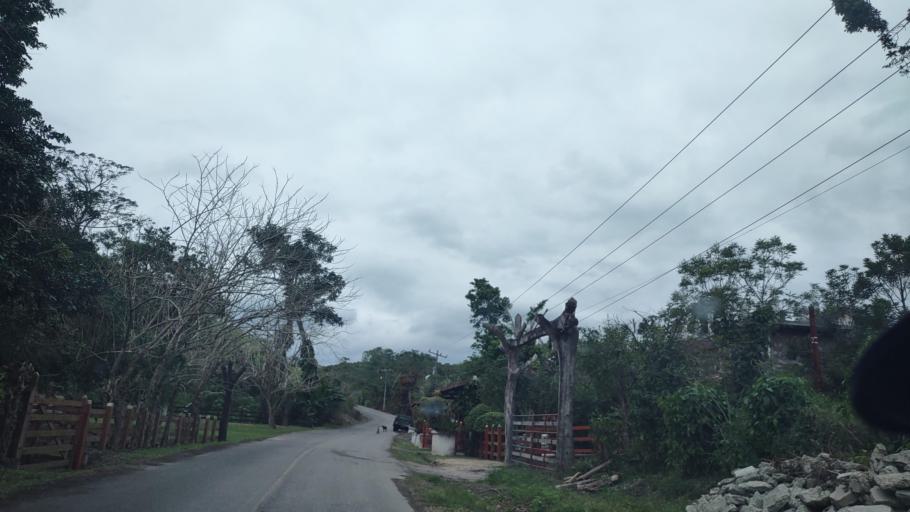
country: MX
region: Veracruz
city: Papantla de Olarte
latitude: 20.4444
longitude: -97.2899
